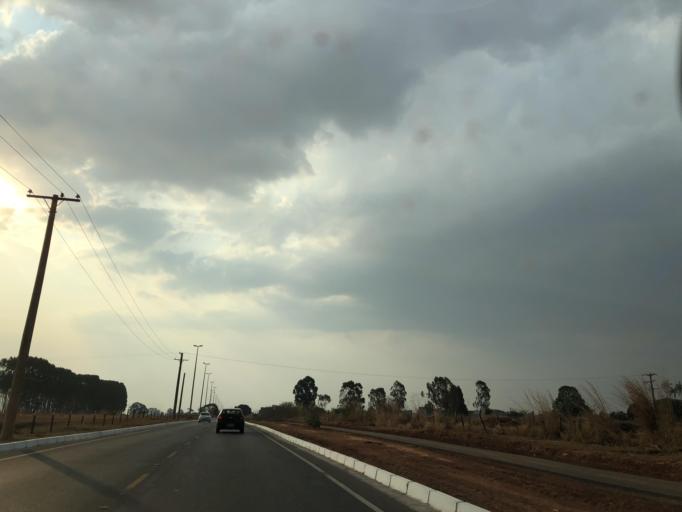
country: BR
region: Federal District
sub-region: Brasilia
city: Brasilia
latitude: -15.9294
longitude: -48.0486
